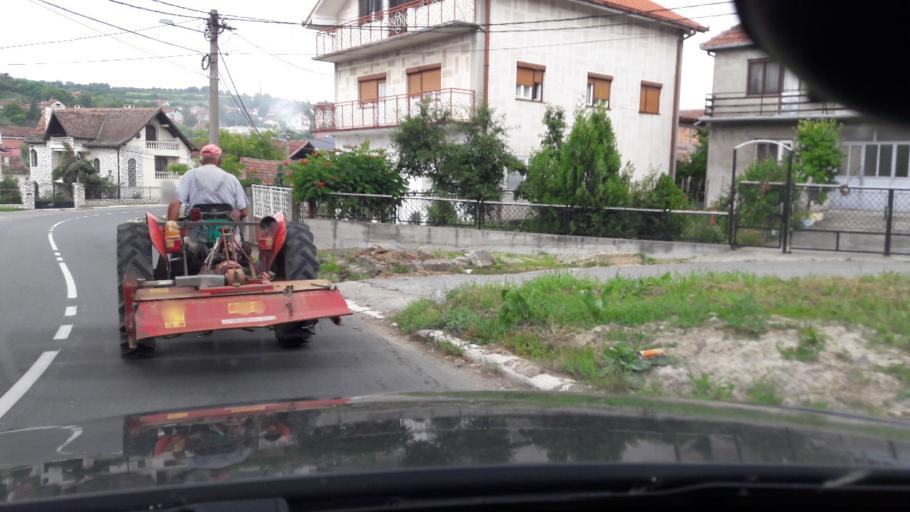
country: RS
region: Central Serbia
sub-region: Belgrade
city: Grocka
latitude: 44.6725
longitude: 20.5982
